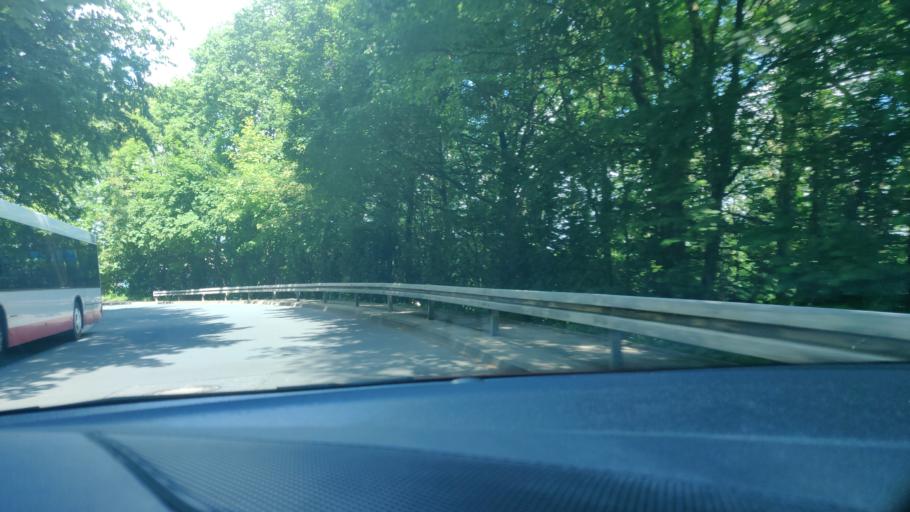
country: DE
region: North Rhine-Westphalia
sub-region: Regierungsbezirk Dusseldorf
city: Heiligenhaus
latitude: 51.3317
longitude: 7.0033
